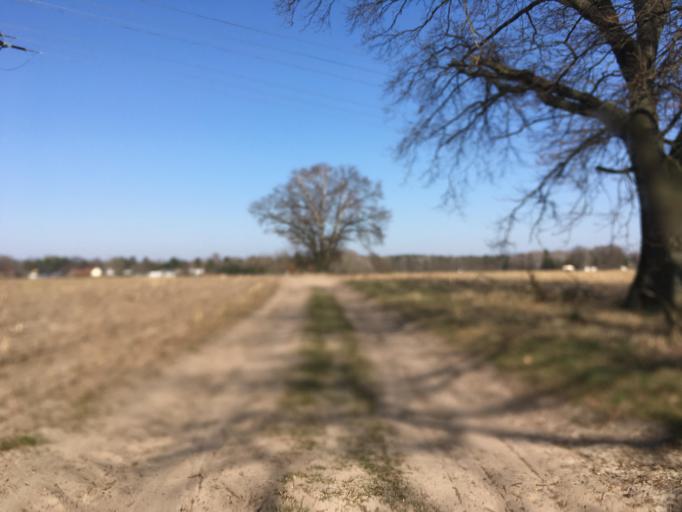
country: DE
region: Berlin
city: Buch
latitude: 52.6753
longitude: 13.4672
